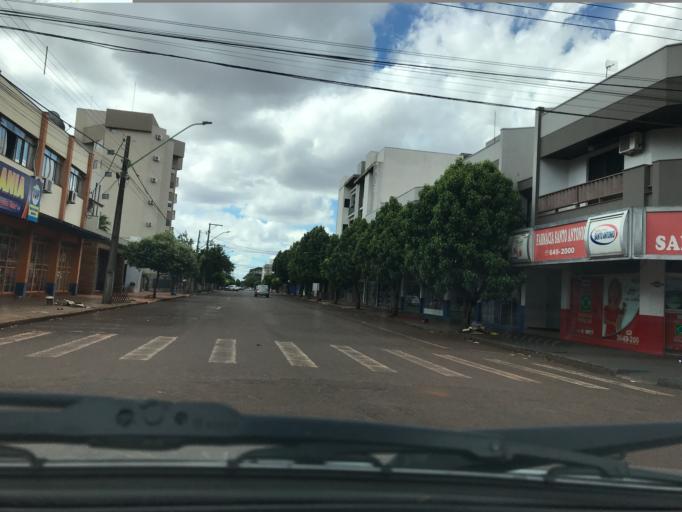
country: BR
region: Parana
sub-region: Palotina
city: Palotina
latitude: -24.2851
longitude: -53.8381
